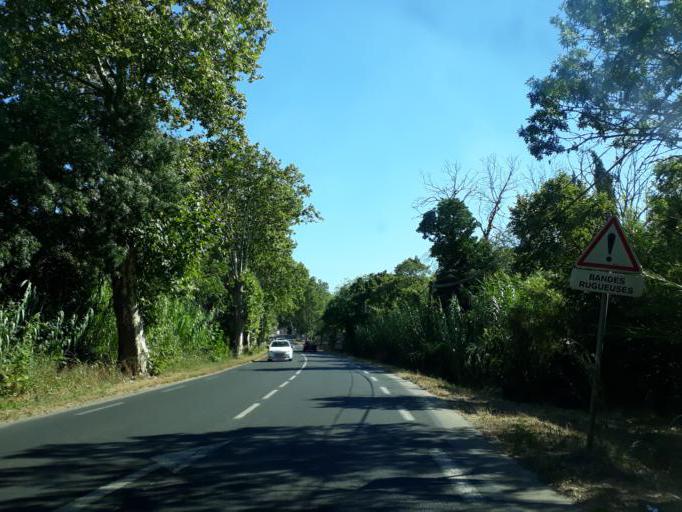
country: FR
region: Languedoc-Roussillon
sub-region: Departement de l'Herault
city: Agde
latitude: 43.3212
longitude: 3.4764
